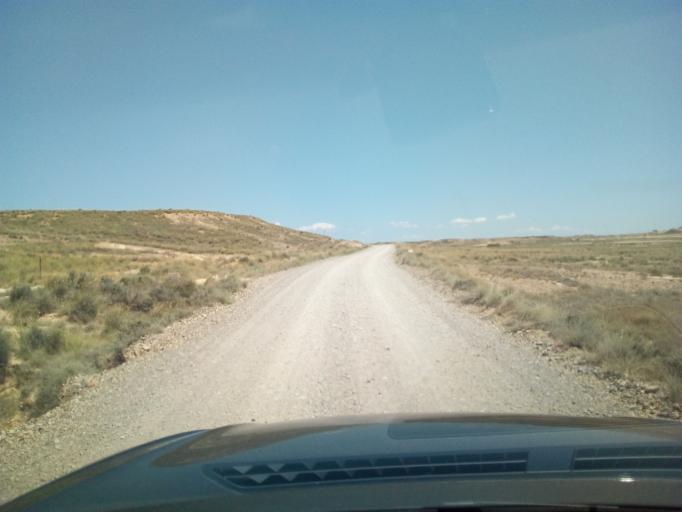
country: ES
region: Navarre
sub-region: Provincia de Navarra
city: Fustinana
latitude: 42.1706
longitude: -1.4216
